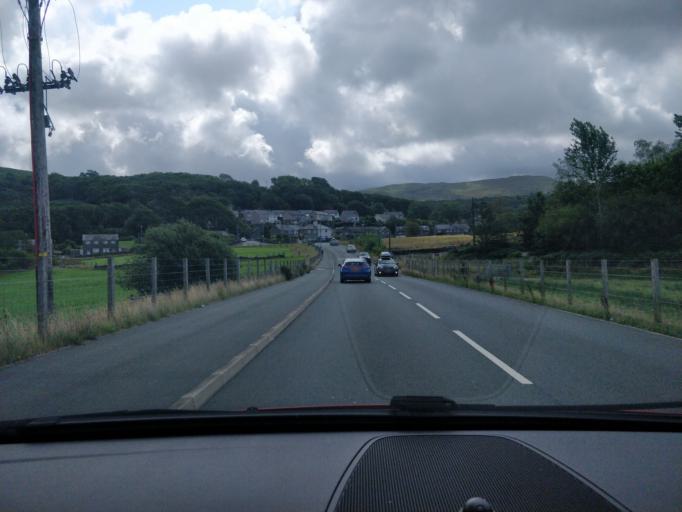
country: GB
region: Wales
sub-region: Gwynedd
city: Penrhyndeudraeth
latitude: 52.9190
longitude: -4.0539
